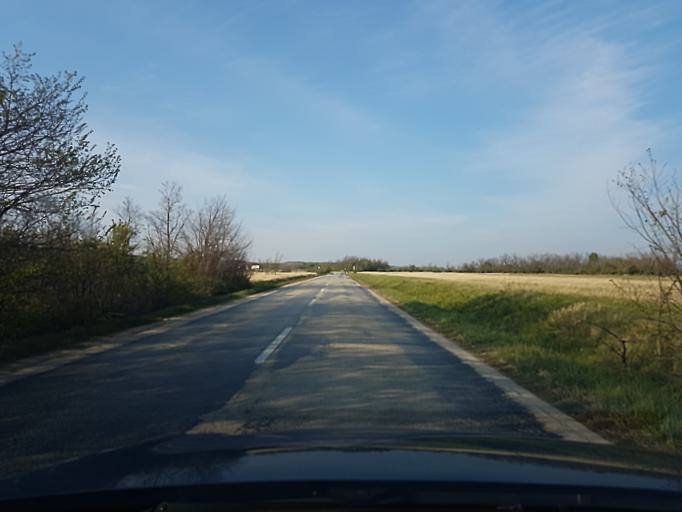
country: HU
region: Fejer
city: Fehervarcsurgo
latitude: 47.3335
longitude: 18.3213
